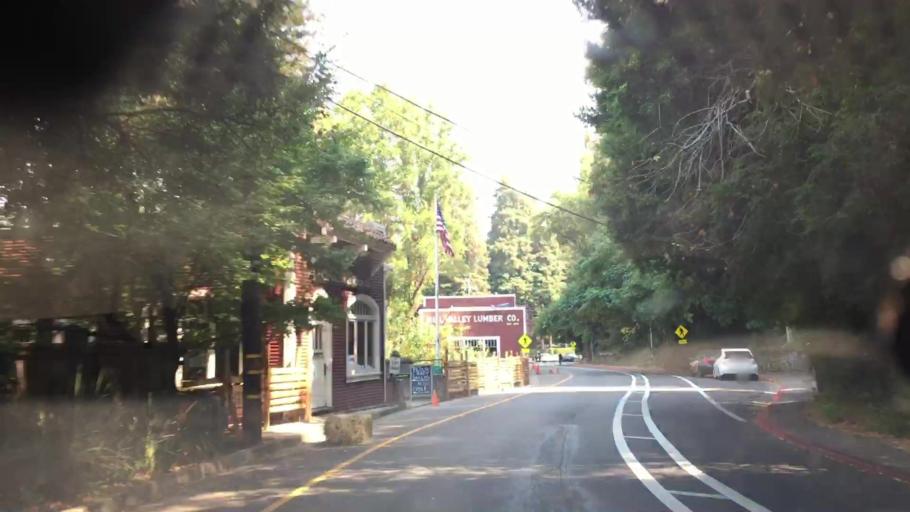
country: US
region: California
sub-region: Marin County
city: Mill Valley
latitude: 37.9037
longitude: -122.5451
